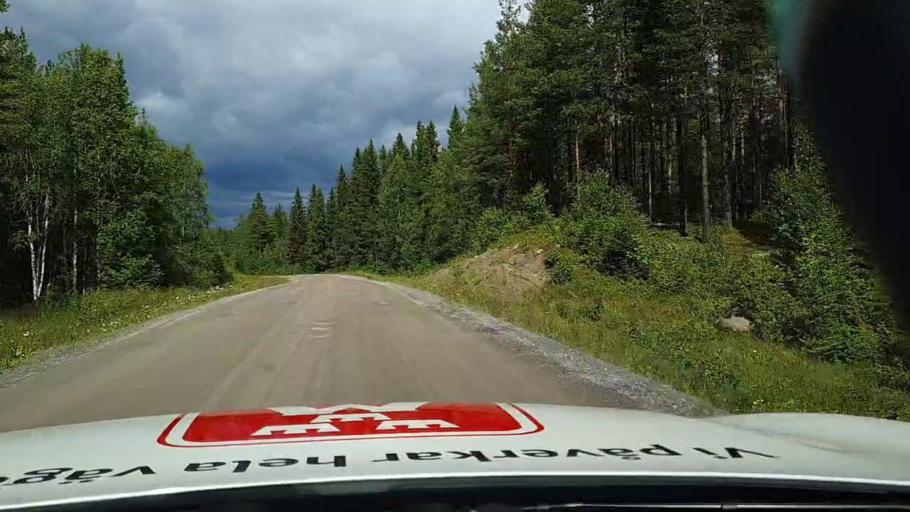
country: SE
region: Vaesternorrland
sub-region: Solleftea Kommun
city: As
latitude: 63.4690
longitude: 16.2816
